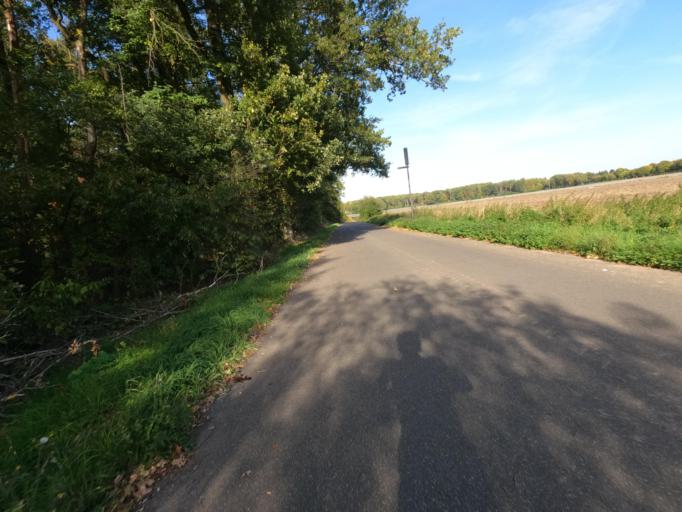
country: DE
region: North Rhine-Westphalia
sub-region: Regierungsbezirk Dusseldorf
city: Niederkruchten
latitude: 51.1558
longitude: 6.2101
